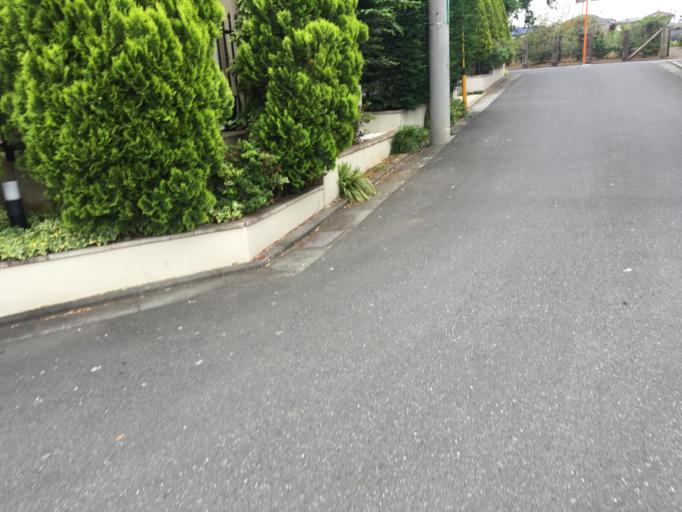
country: JP
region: Tokyo
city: Kokubunji
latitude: 35.6935
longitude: 139.4782
